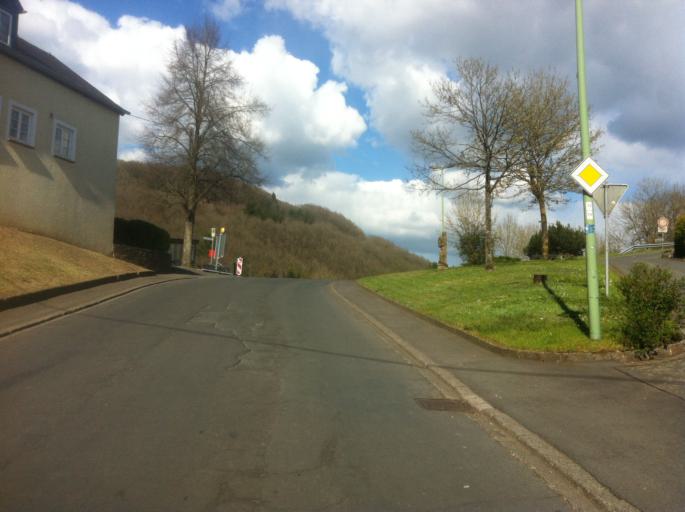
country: DE
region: Rheinland-Pfalz
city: Olmscheid
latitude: 50.0806
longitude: 6.2134
